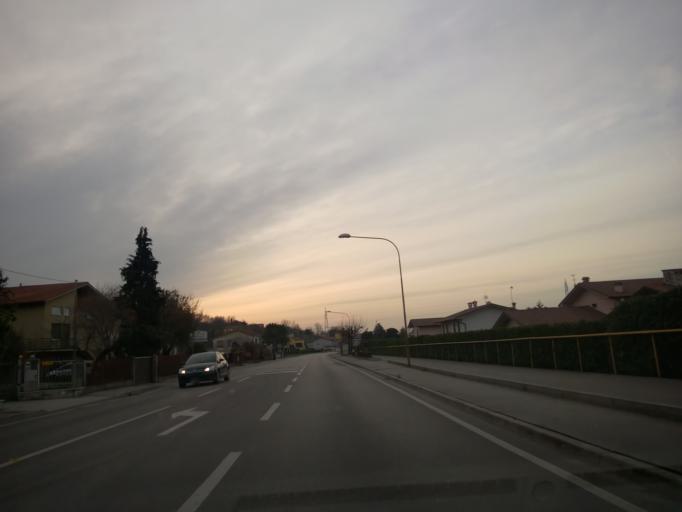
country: IT
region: Veneto
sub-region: Provincia di Vicenza
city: Carre
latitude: 45.7434
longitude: 11.4601
